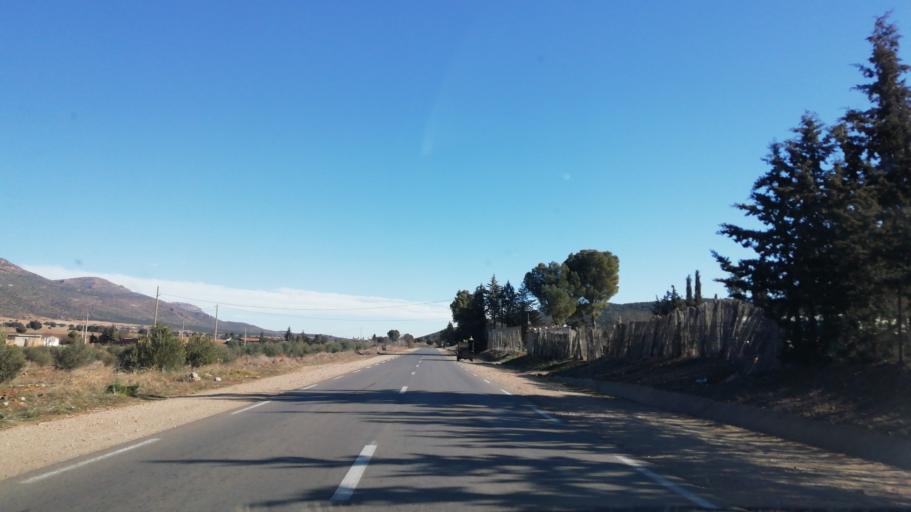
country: DZ
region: Tlemcen
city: Sebdou
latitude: 34.6816
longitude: -1.2557
